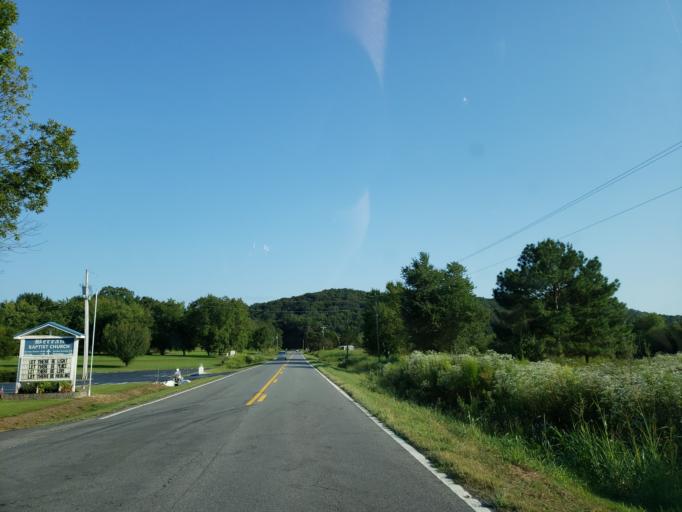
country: US
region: Tennessee
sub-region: Bradley County
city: Wildwood Lake
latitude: 35.0078
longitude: -84.7868
